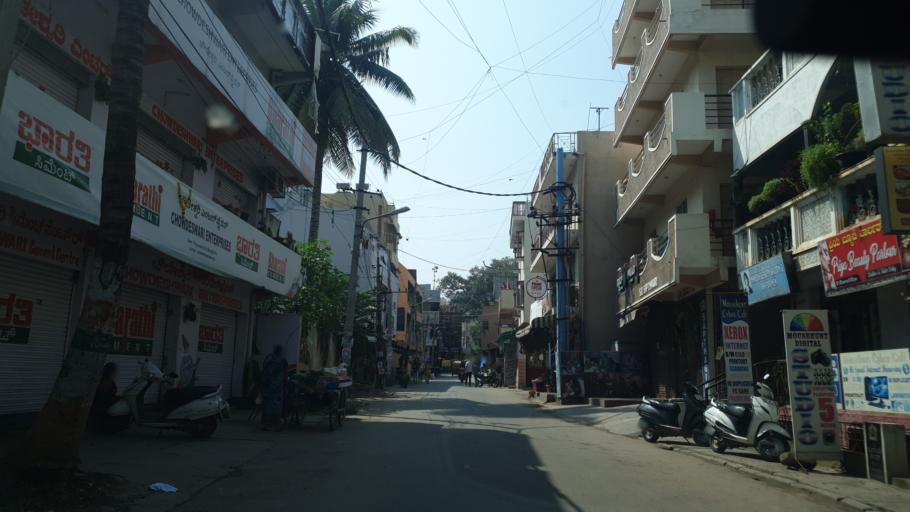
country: IN
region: Karnataka
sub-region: Bangalore Urban
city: Bangalore
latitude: 12.9764
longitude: 77.6660
